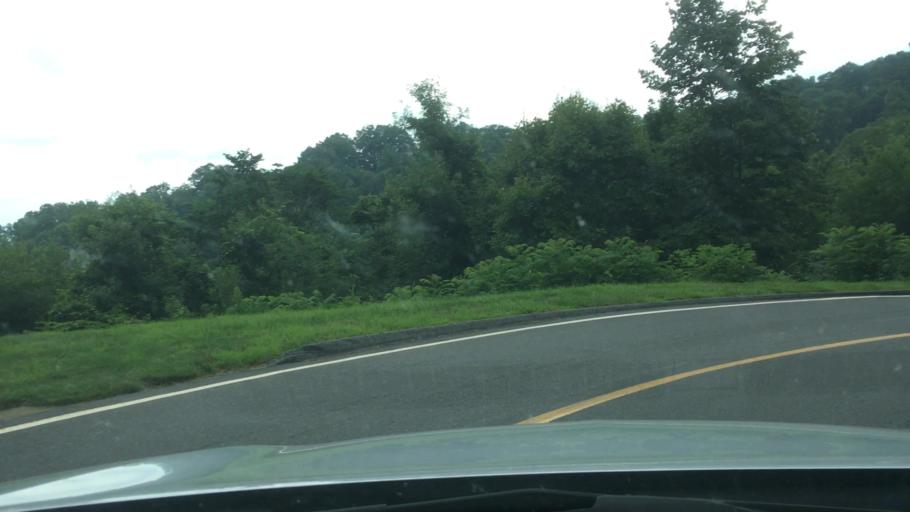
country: US
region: North Carolina
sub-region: Yancey County
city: Burnsville
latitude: 35.8779
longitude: -82.3497
